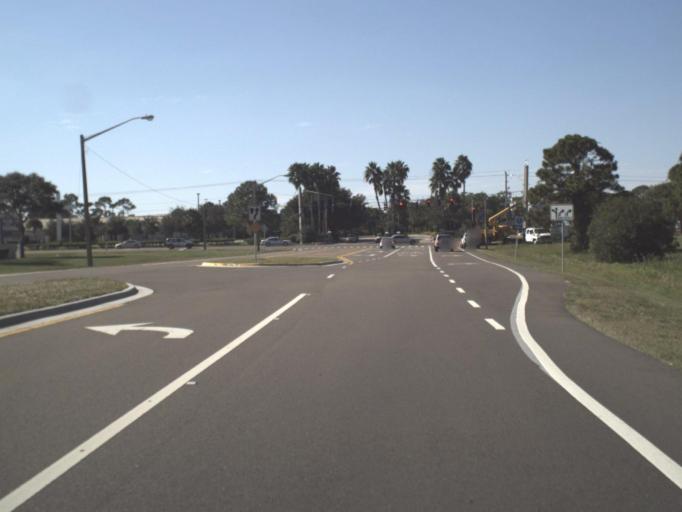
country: US
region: Florida
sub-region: Brevard County
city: South Patrick Shores
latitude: 28.2032
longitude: -80.6705
